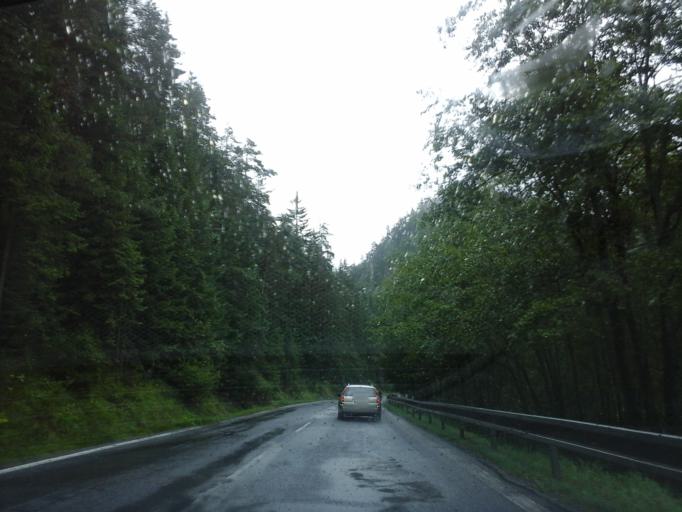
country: SK
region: Presovsky
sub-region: Okres Poprad
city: Poprad
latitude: 48.9294
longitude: 20.2829
